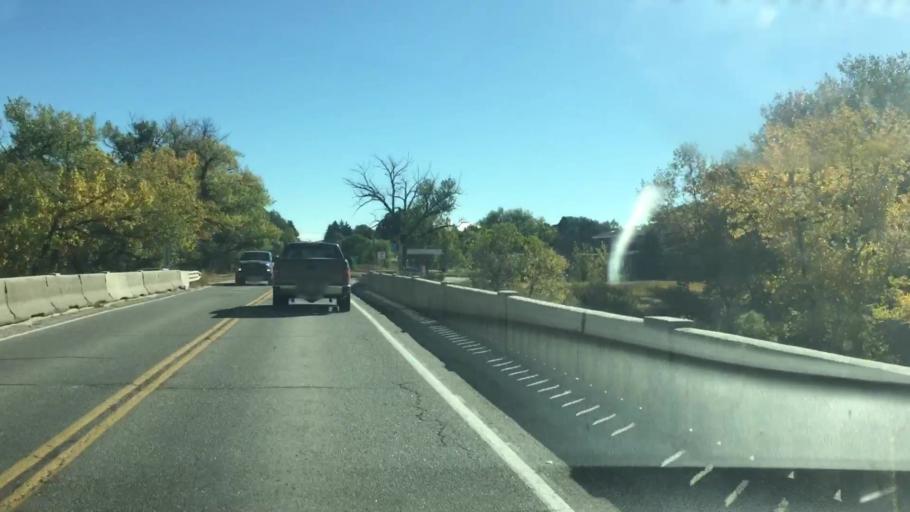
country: US
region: Colorado
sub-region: Elbert County
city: Kiowa
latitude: 39.3465
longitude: -104.4706
